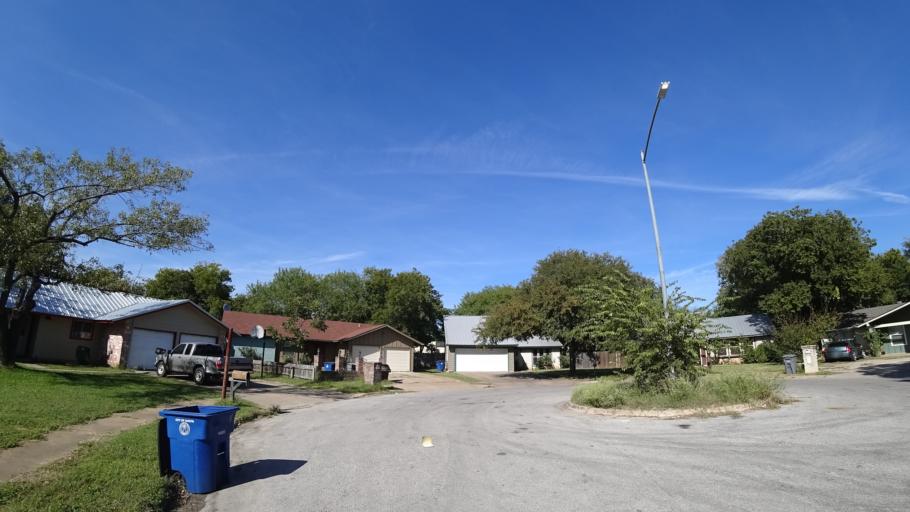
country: US
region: Texas
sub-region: Travis County
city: Austin
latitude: 30.1966
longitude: -97.7456
